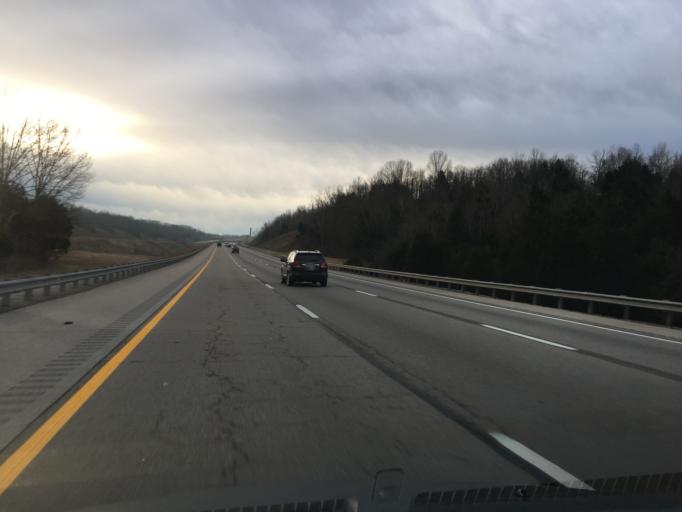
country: US
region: Kentucky
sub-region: Grant County
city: Williamstown
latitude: 38.5431
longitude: -84.5956
